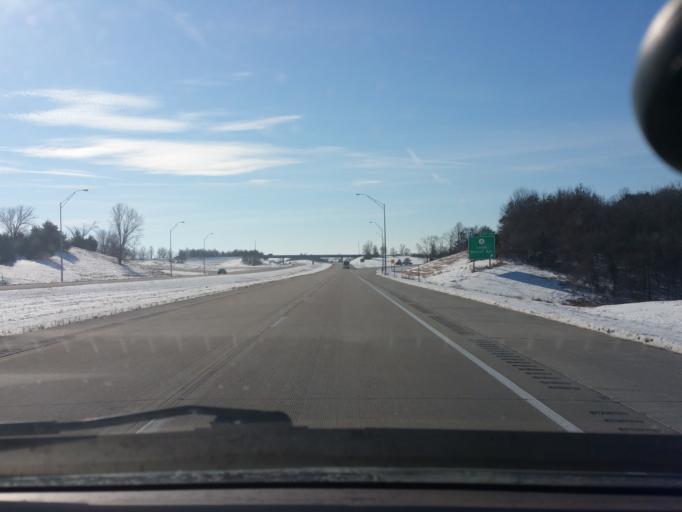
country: US
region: Iowa
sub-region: Decatur County
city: Leon
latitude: 40.7451
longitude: -93.8412
